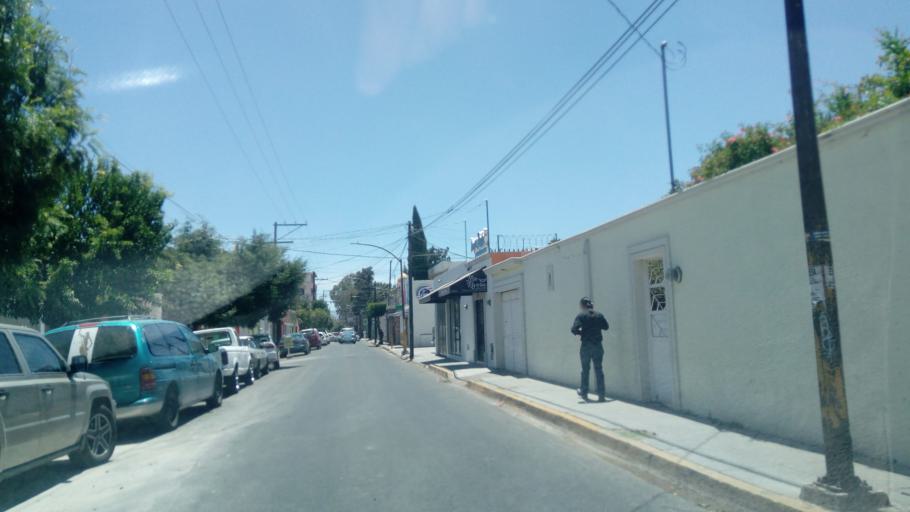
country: MX
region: Durango
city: Victoria de Durango
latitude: 24.0293
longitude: -104.6618
